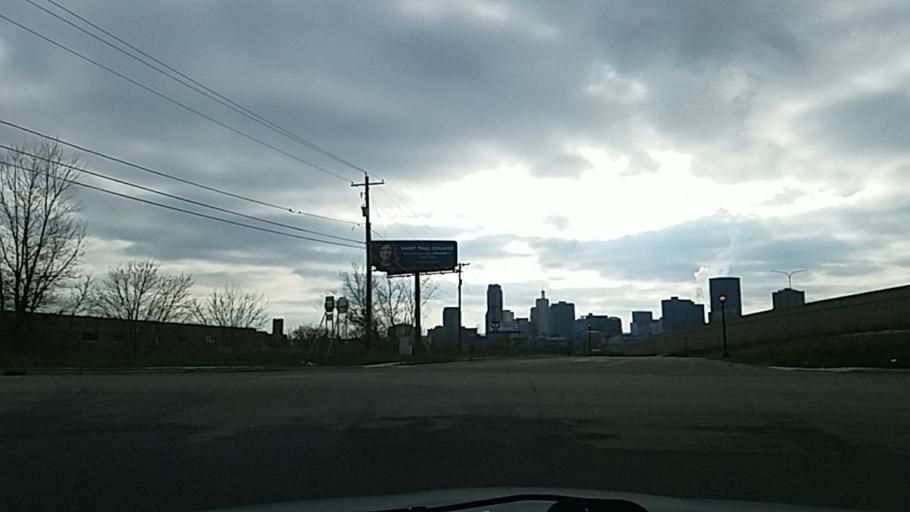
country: US
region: Minnesota
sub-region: Ramsey County
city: Saint Paul
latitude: 44.9613
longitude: -93.0896
